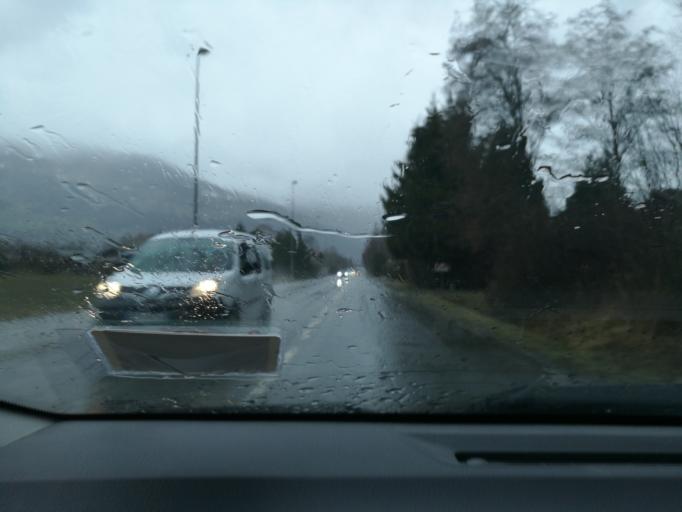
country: FR
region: Rhone-Alpes
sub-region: Departement de la Haute-Savoie
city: Domancy
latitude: 45.9339
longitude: 6.6500
